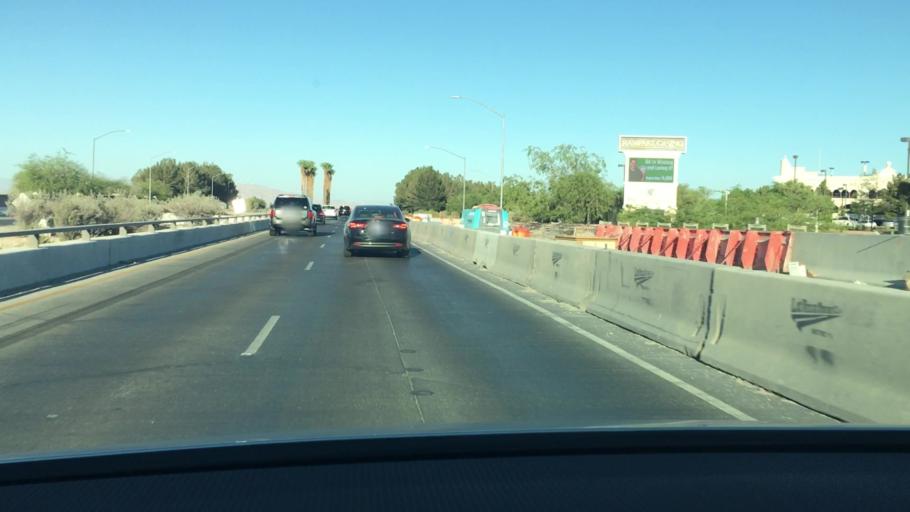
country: US
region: Nevada
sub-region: Clark County
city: Summerlin South
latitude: 36.1782
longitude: -115.2920
